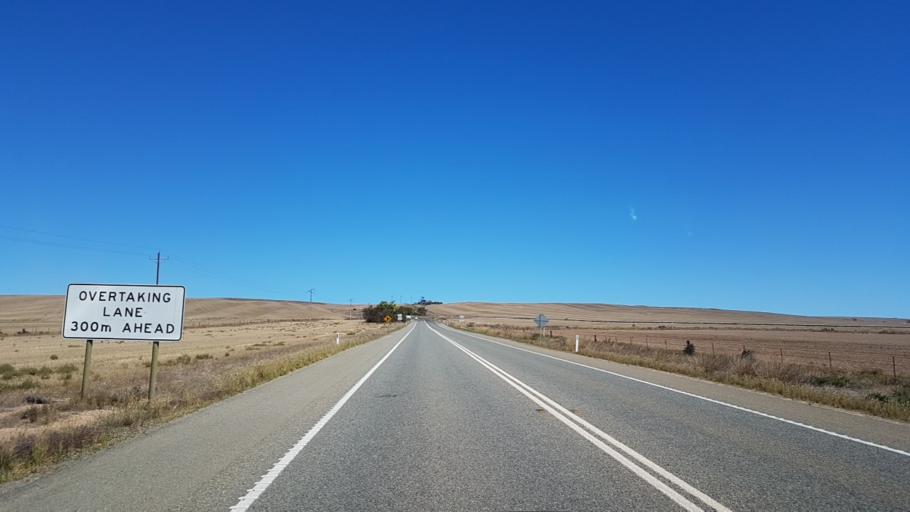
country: AU
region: South Australia
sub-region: Wakefield
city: Balaklava
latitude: -34.0701
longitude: 138.0680
